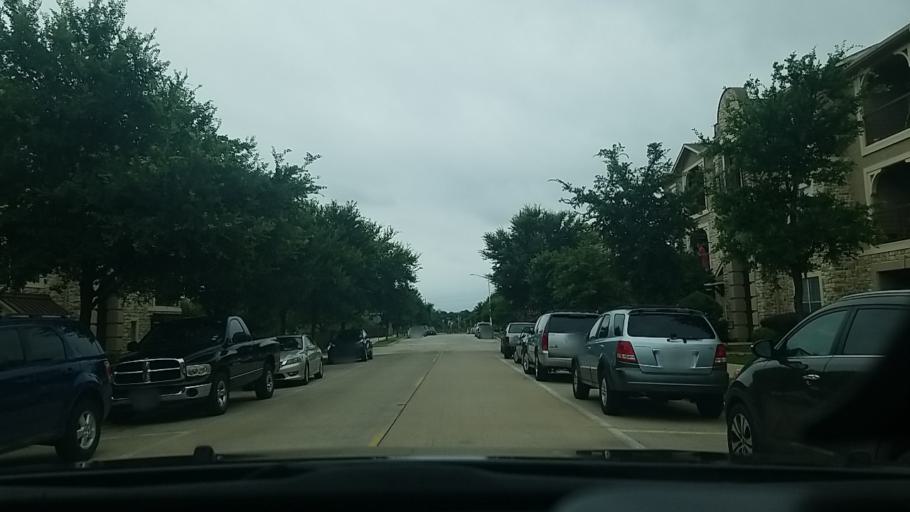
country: US
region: Texas
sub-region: Denton County
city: Corinth
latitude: 33.1853
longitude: -97.0921
